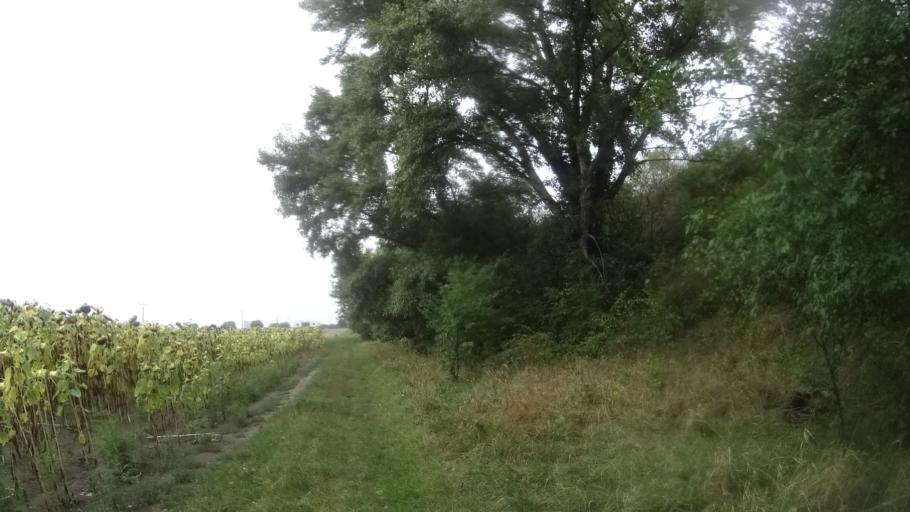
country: SK
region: Nitriansky
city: Komarno
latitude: 47.7621
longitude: 18.0872
